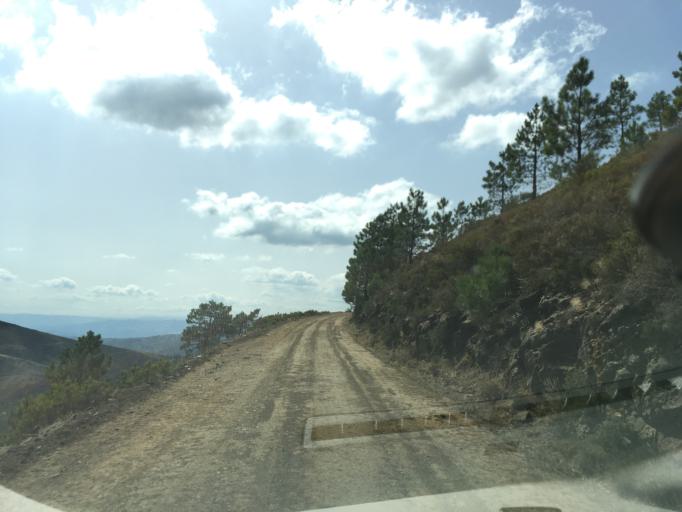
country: PT
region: Braga
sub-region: Celorico de Basto
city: Celorico de Basto
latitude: 41.2940
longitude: -7.9398
